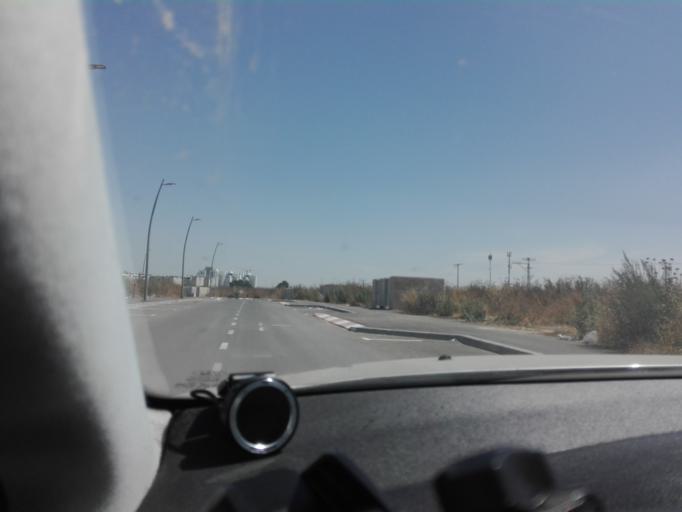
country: IL
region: Central District
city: Bene 'Ayish
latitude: 31.7338
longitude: 34.7347
